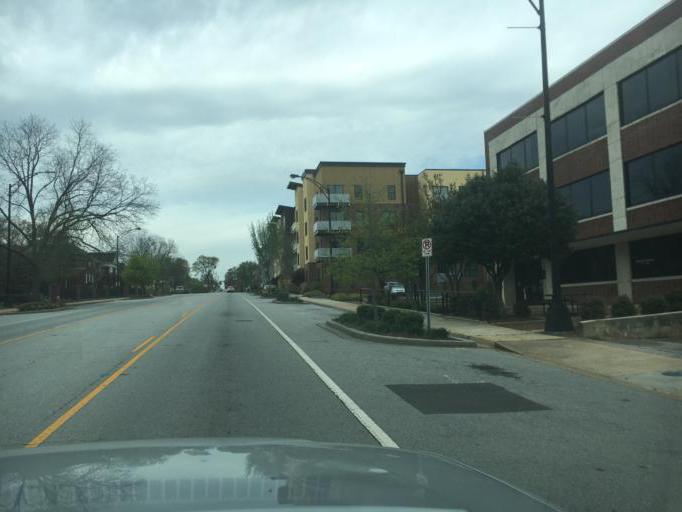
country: US
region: South Carolina
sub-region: Greenville County
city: Greenville
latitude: 34.8594
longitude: -82.3952
